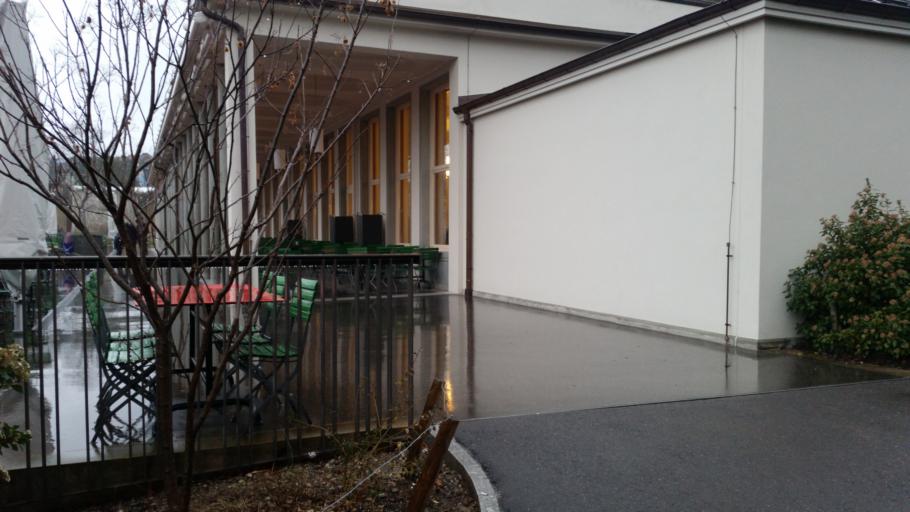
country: CH
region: Basel-City
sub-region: Basel-Stadt
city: Basel
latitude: 47.5478
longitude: 7.5783
